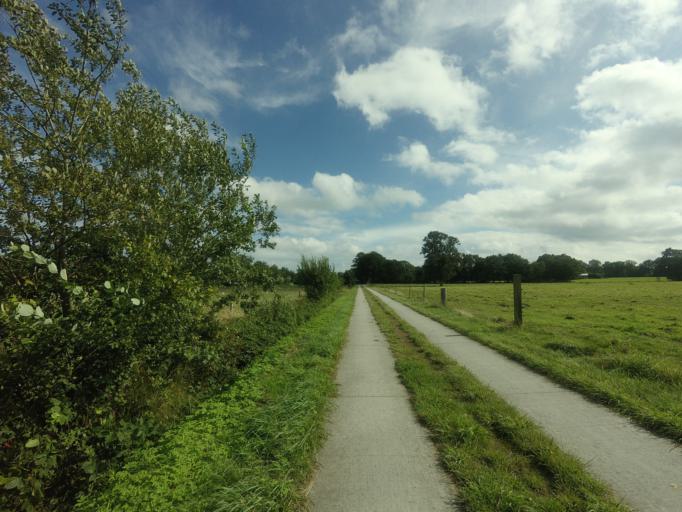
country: NL
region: Friesland
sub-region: Gemeente Heerenveen
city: Jubbega
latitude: 53.0008
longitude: 6.2922
